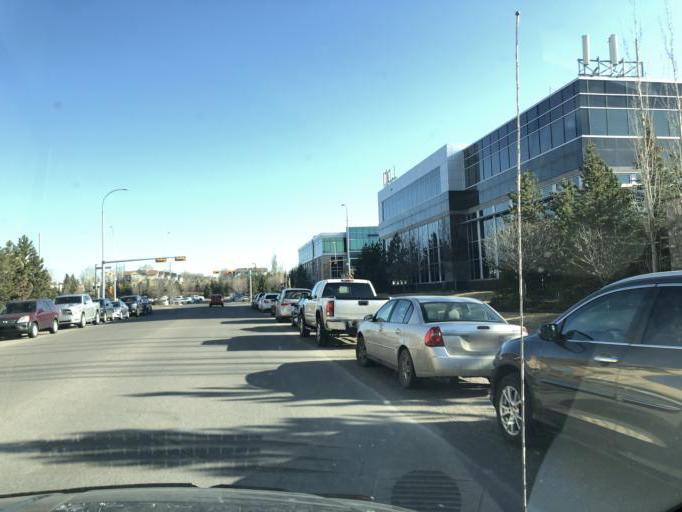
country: CA
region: Alberta
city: Calgary
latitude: 50.9624
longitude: -114.0072
